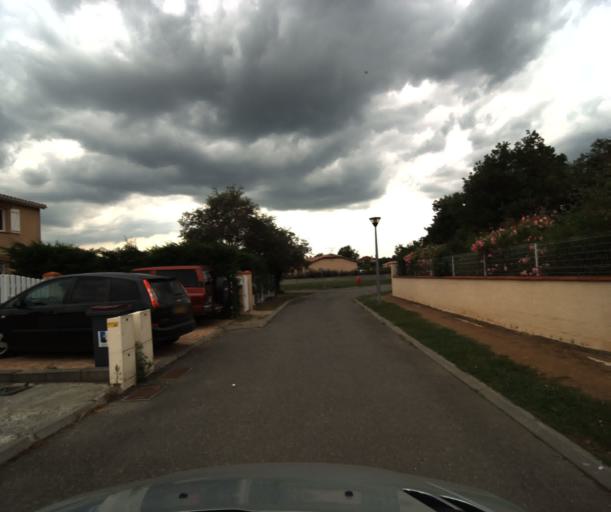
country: FR
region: Midi-Pyrenees
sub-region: Departement de la Haute-Garonne
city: Lherm
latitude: 43.4647
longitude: 1.2094
